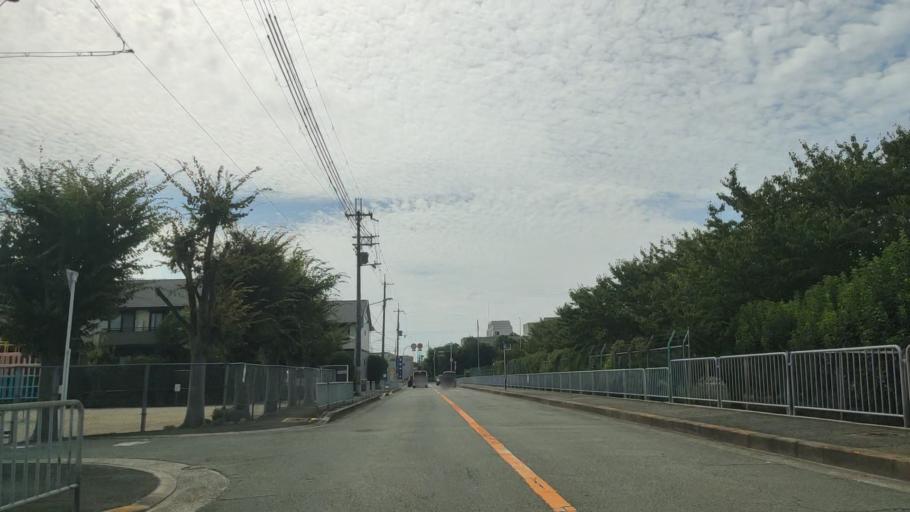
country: JP
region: Osaka
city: Ikeda
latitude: 34.8123
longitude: 135.4350
